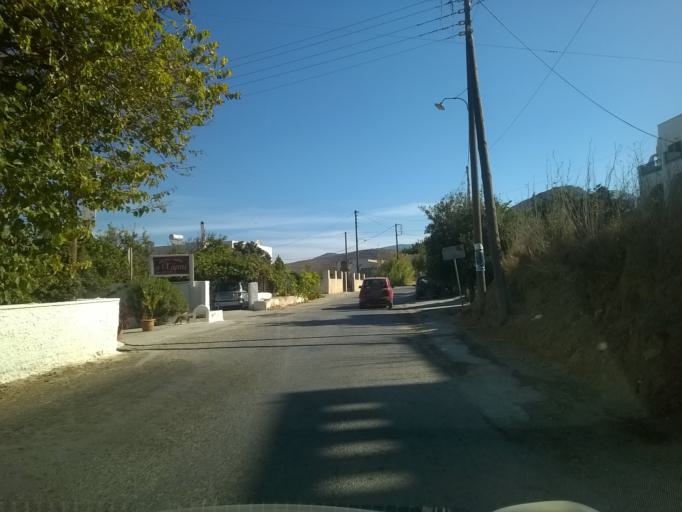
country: GR
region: South Aegean
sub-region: Nomos Kykladon
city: Naxos
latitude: 37.1162
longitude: 25.4329
